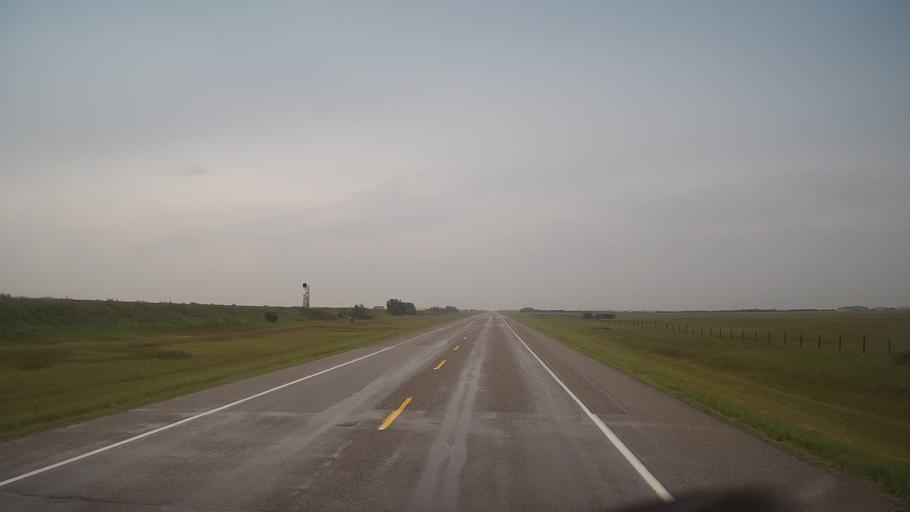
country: CA
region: Saskatchewan
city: Wilkie
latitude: 52.2172
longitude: -108.5069
